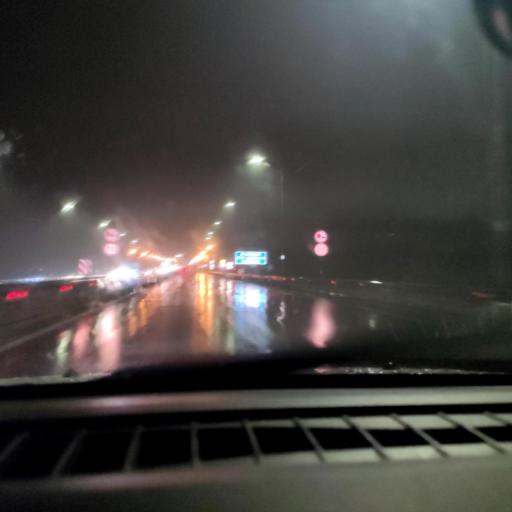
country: RU
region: Voronezj
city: Pridonskoy
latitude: 51.6499
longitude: 39.0801
